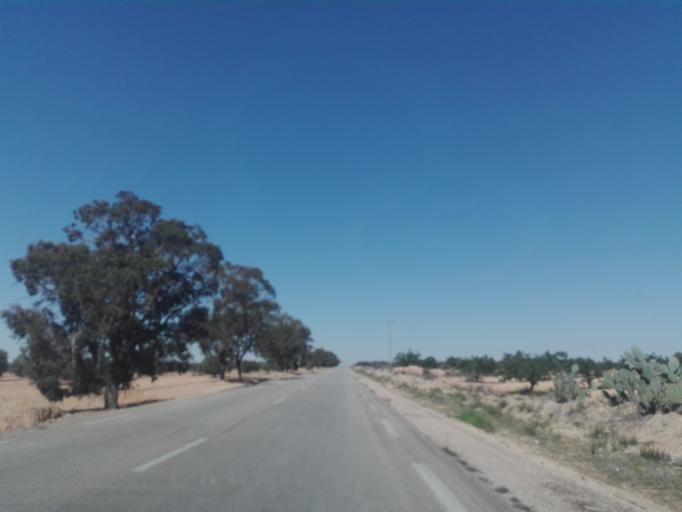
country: TN
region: Safaqis
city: Bi'r `Ali Bin Khalifah
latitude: 34.7579
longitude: 10.3136
